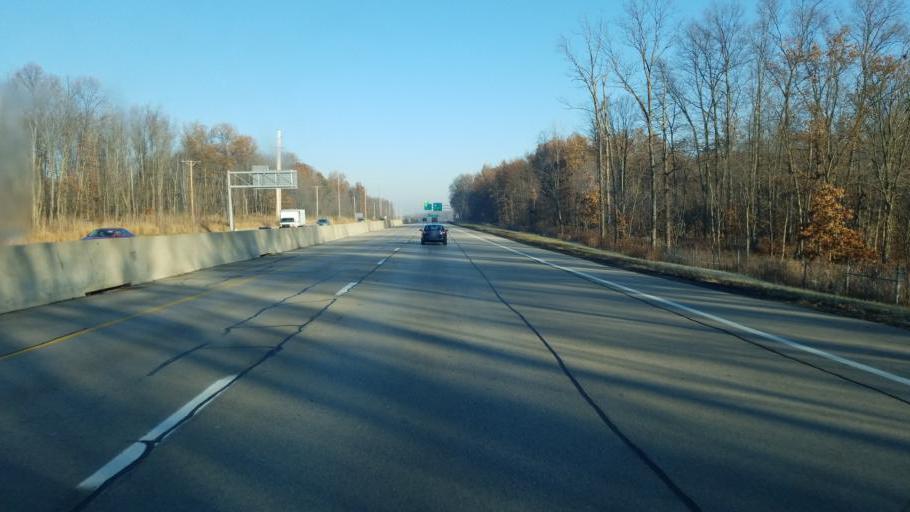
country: US
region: Ohio
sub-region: Summit County
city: Boston Heights
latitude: 41.2694
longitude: -81.5028
